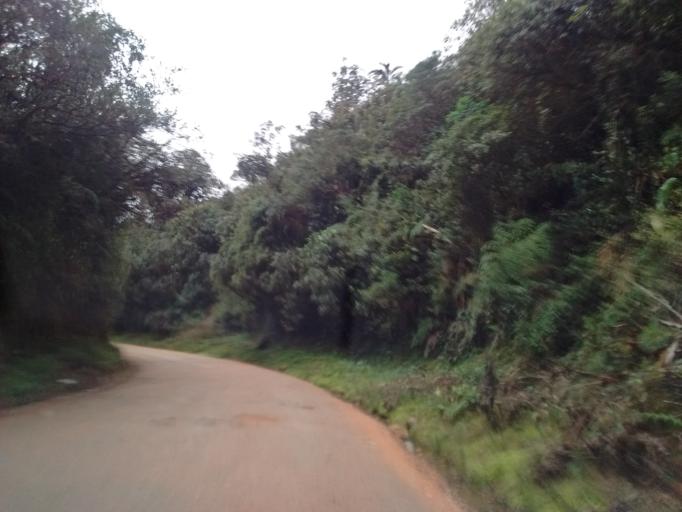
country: CO
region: Huila
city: Isnos
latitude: 2.1346
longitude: -76.3798
